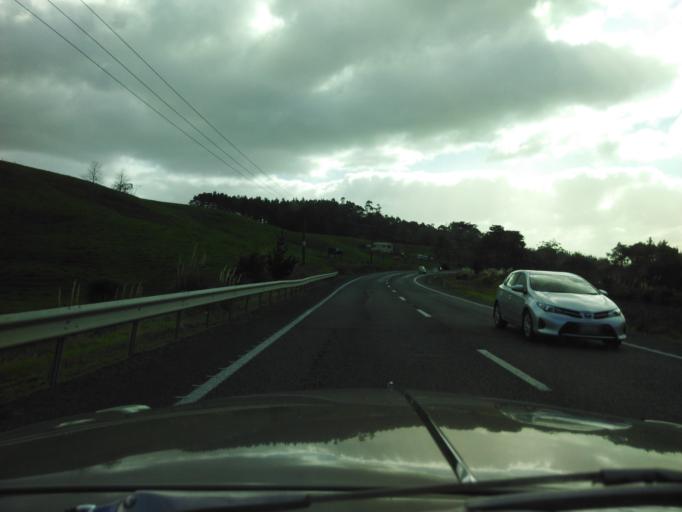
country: NZ
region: Auckland
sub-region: Auckland
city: Wellsford
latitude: -36.2648
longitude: 174.5110
